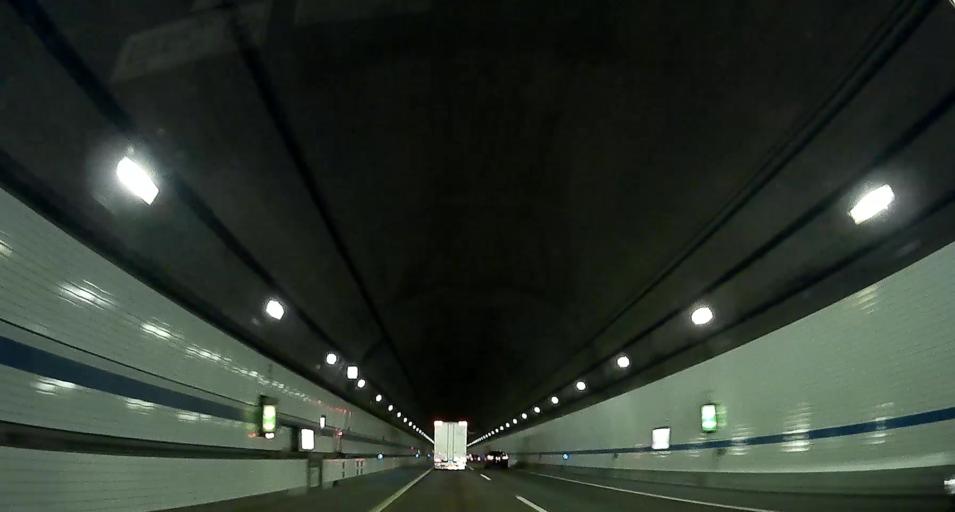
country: JP
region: Chiba
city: Kisarazu
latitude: 35.4689
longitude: 139.8674
